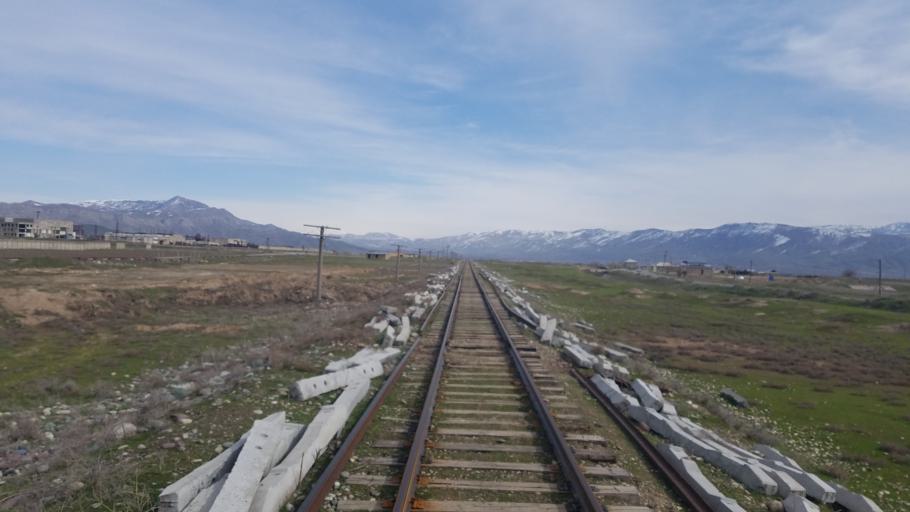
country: TJ
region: Khatlon
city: Yovon
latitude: 38.2826
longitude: 68.9313
